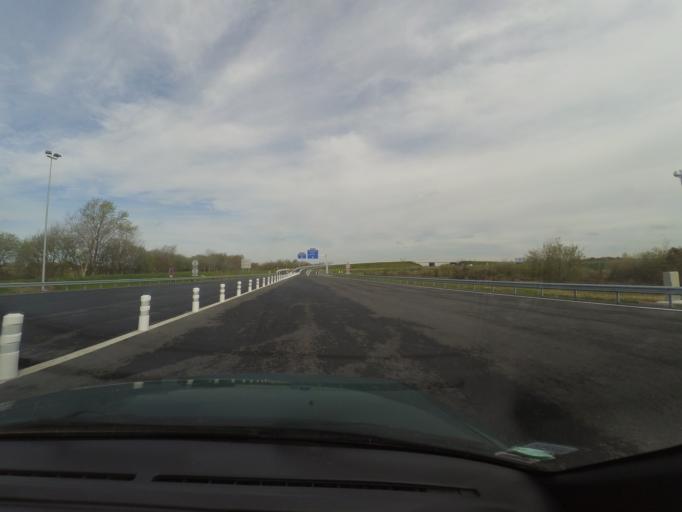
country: FR
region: Pays de la Loire
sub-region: Departement de la Loire-Atlantique
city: Aigrefeuille-sur-Maine
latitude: 47.0697
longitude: -1.4376
